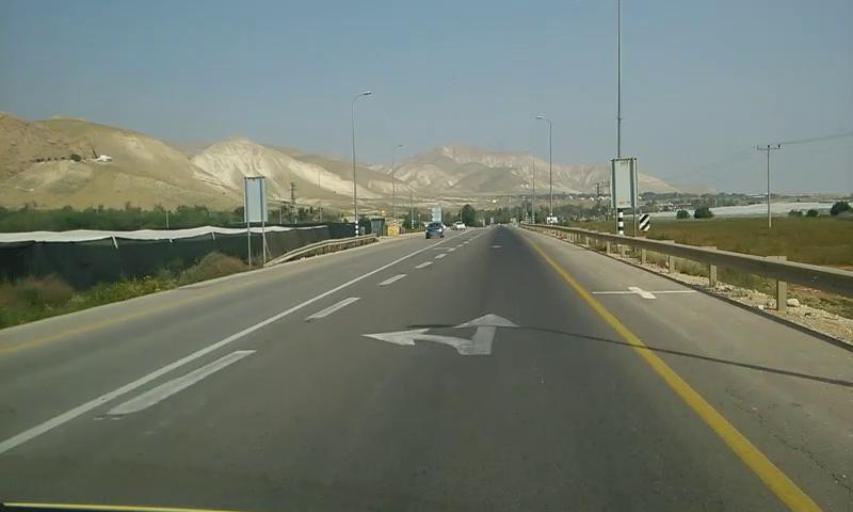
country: PS
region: West Bank
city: Al Fasayil
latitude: 32.0476
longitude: 35.4635
